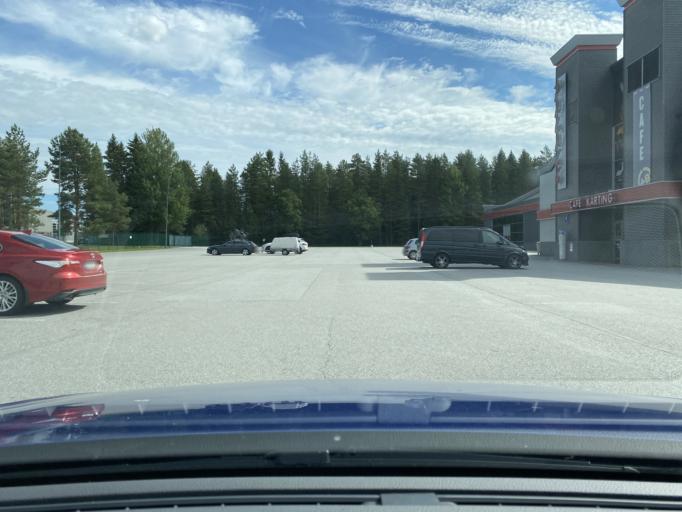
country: FI
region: Southern Ostrobothnia
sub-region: Seinaejoki
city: Alahaermae
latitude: 63.2275
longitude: 22.8599
